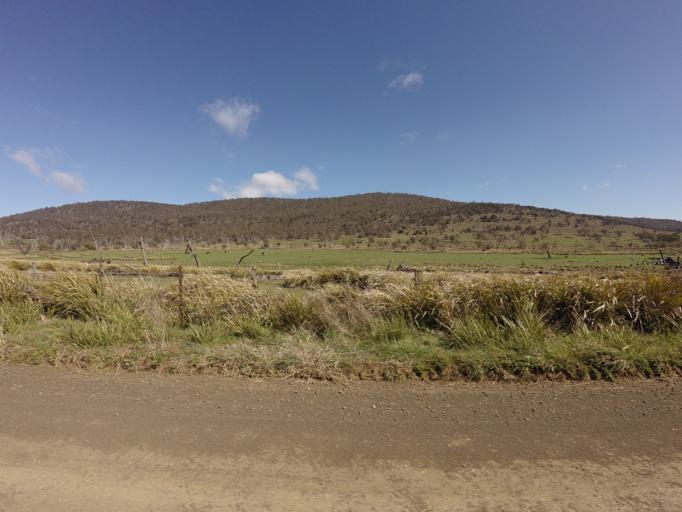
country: AU
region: Tasmania
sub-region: Northern Midlands
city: Evandale
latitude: -41.9349
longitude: 147.4189
